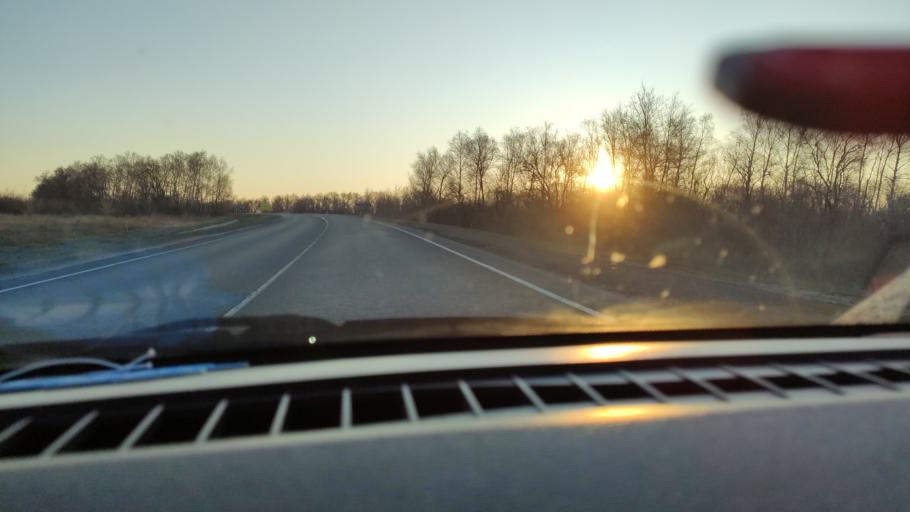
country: RU
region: Saratov
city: Sinodskoye
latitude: 51.9350
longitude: 46.5896
